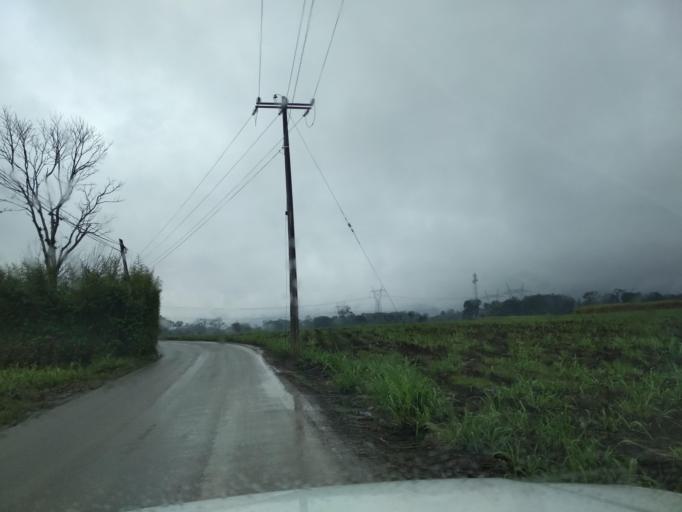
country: MX
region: Veracruz
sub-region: Amatlan de los Reyes
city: Centro de Readaptacion Social
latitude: 18.8317
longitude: -96.9299
